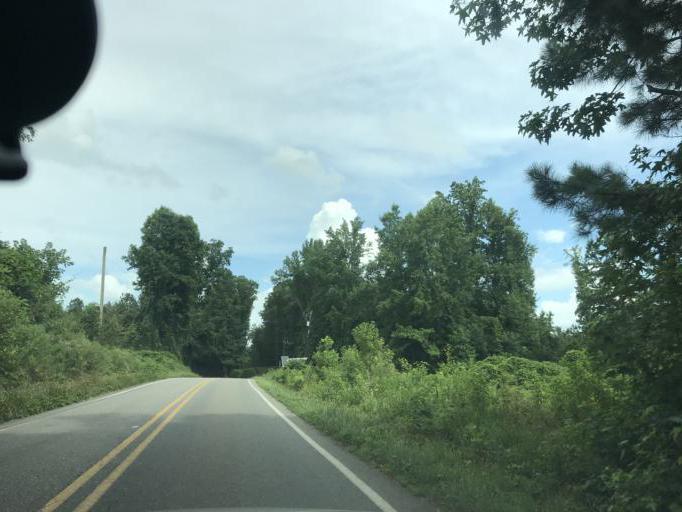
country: US
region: Georgia
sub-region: Cherokee County
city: Ball Ground
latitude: 34.3301
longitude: -84.2607
